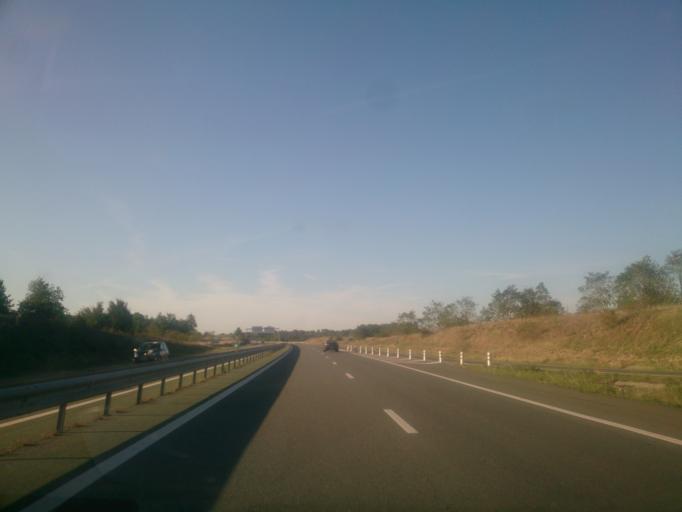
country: FR
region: Midi-Pyrenees
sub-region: Departement du Lot
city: Le Vigan
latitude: 44.6994
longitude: 1.5732
